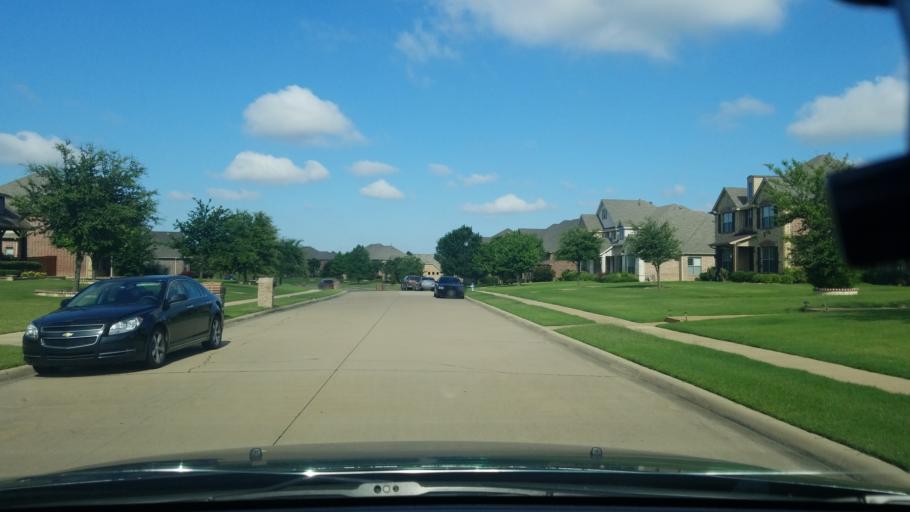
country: US
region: Texas
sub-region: Dallas County
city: Sunnyvale
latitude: 32.8062
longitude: -96.5625
